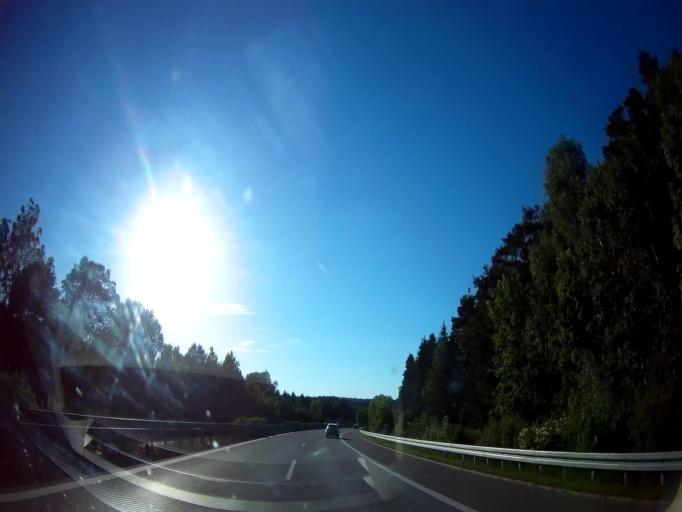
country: DE
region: Bavaria
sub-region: Upper Palatinate
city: Sinzing
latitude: 48.9942
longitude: 12.0077
